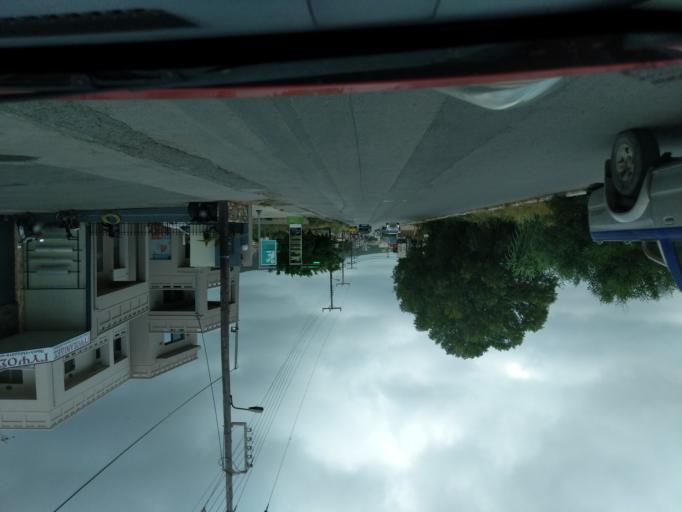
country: GR
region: Crete
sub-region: Nomos Chanias
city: Kissamos
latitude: 35.4987
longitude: 23.6460
